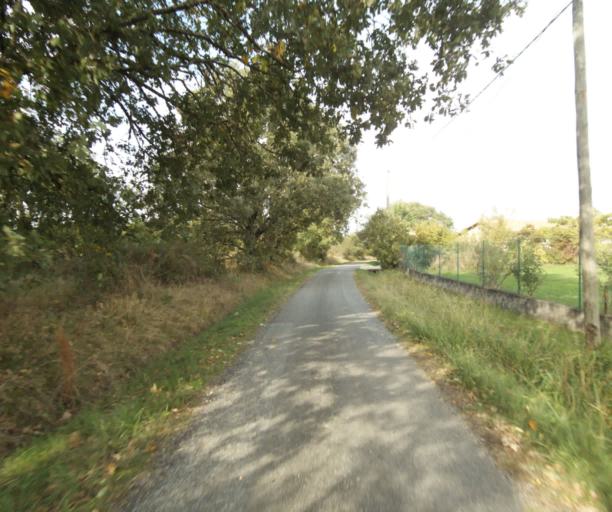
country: FR
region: Midi-Pyrenees
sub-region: Departement du Tarn-et-Garonne
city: Campsas
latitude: 43.9141
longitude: 1.3231
